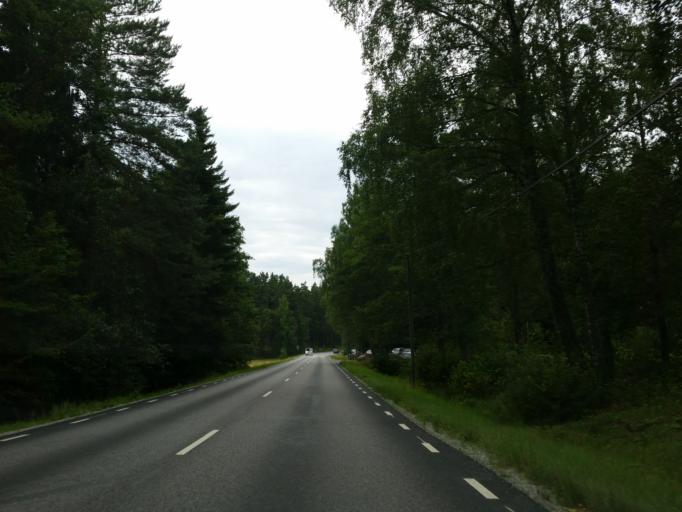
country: SE
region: Stockholm
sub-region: Salems Kommun
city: Ronninge
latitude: 59.2241
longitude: 17.6791
